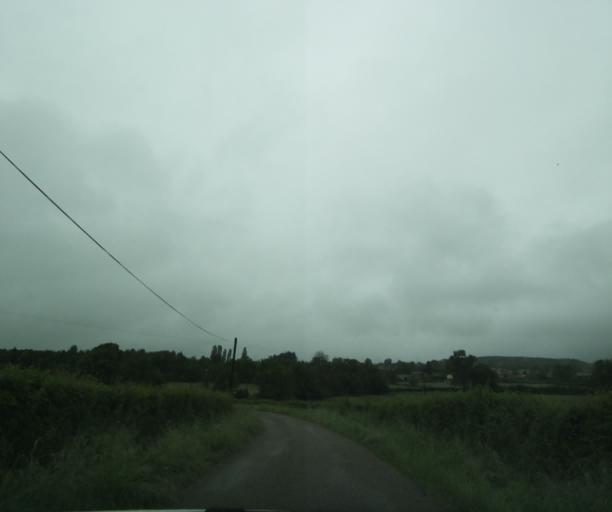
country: FR
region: Bourgogne
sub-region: Departement de Saone-et-Loire
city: Charolles
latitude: 46.3880
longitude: 4.3217
